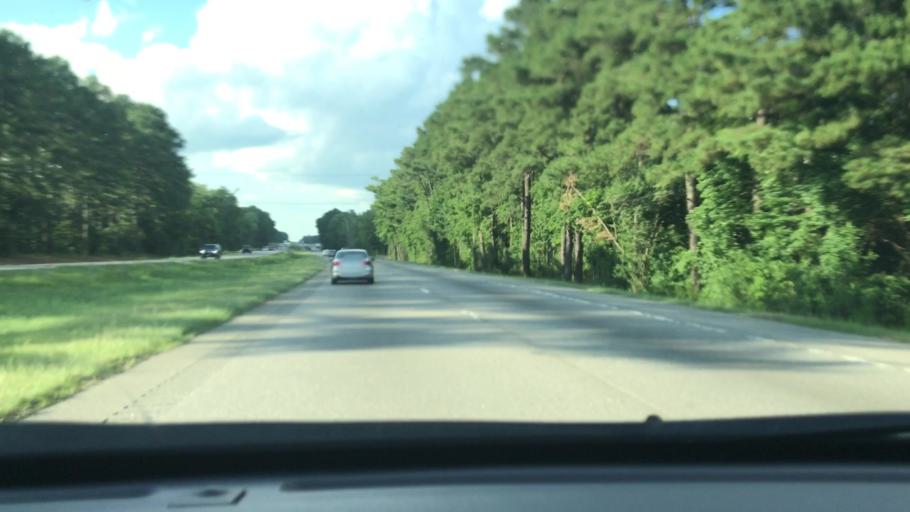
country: US
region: North Carolina
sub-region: Robeson County
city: Saint Pauls
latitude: 34.8552
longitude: -78.9663
